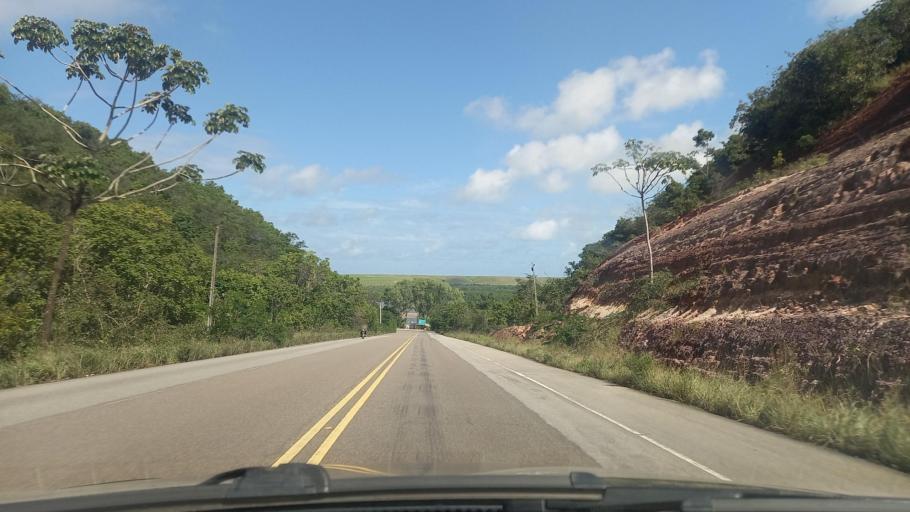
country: BR
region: Alagoas
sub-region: Marechal Deodoro
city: Marechal Deodoro
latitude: -9.8334
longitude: -35.9293
